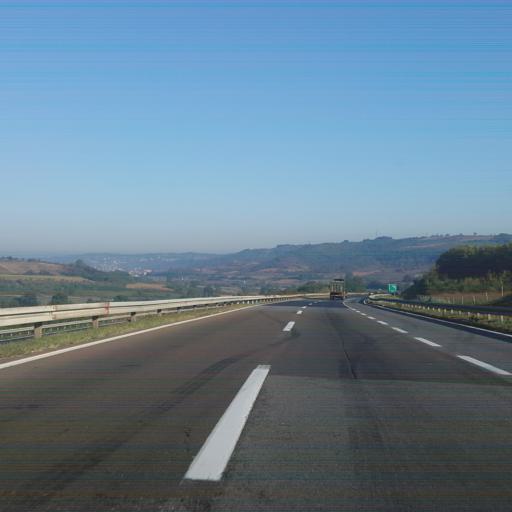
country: RS
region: Central Serbia
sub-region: Belgrade
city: Grocka
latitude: 44.6443
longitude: 20.6295
